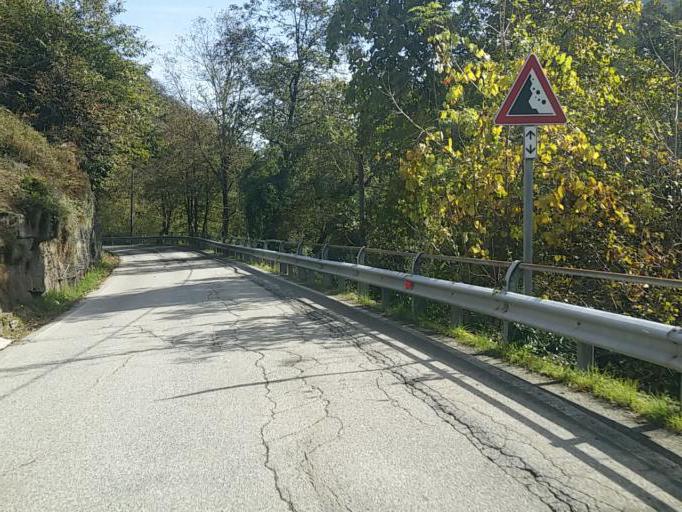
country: IT
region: Piedmont
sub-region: Provincia Verbano-Cusio-Ossola
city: Cavaglio-Spoccia
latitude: 46.0678
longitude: 8.6188
